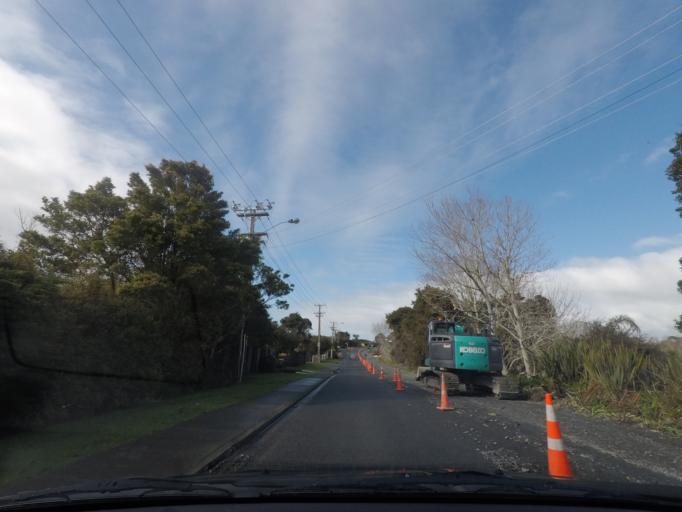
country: NZ
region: Auckland
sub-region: Auckland
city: Warkworth
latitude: -36.4354
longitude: 174.7397
